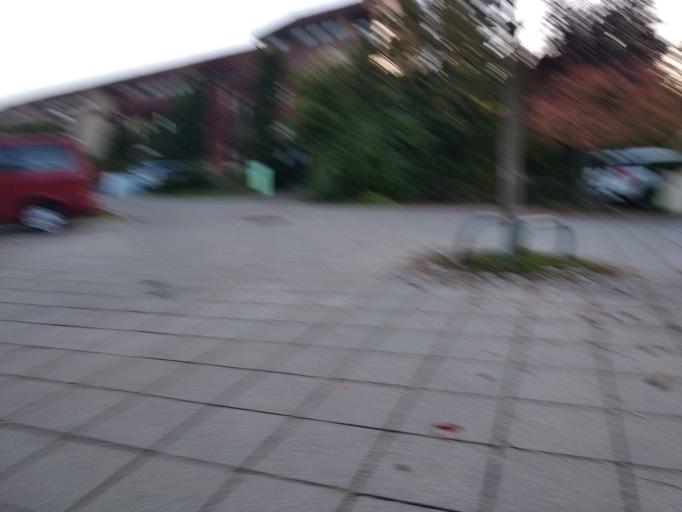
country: DE
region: Bavaria
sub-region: Upper Bavaria
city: Kirchheim bei Muenchen
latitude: 48.1652
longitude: 11.7604
